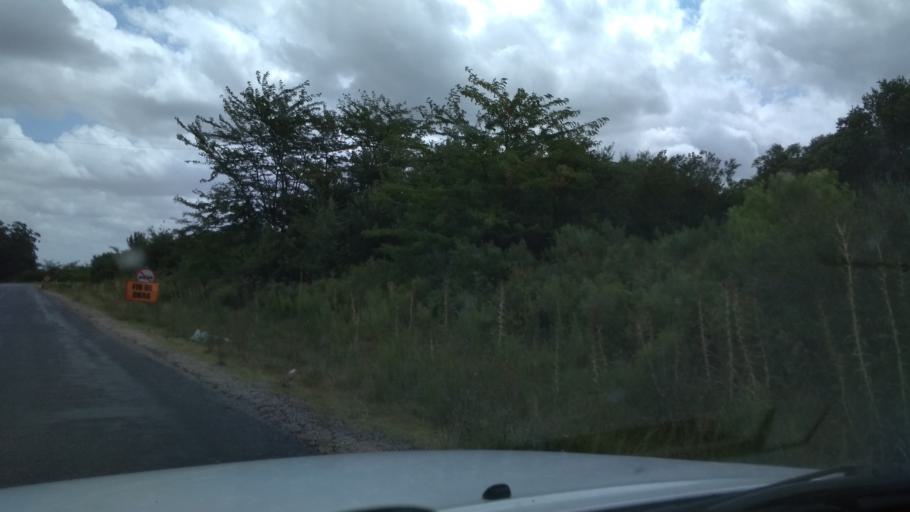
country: UY
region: Canelones
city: San Ramon
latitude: -34.2728
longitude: -55.9464
